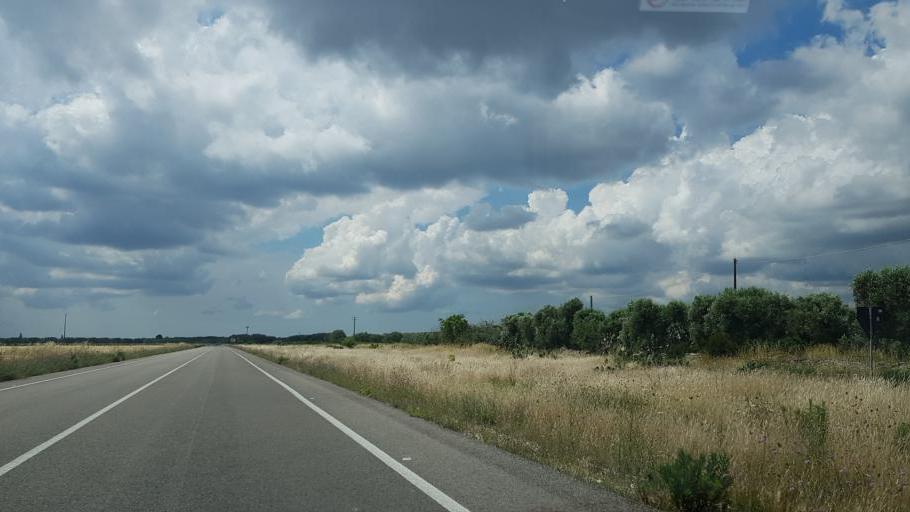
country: IT
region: Apulia
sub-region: Provincia di Brindisi
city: Mesagne
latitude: 40.5038
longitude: 17.8279
